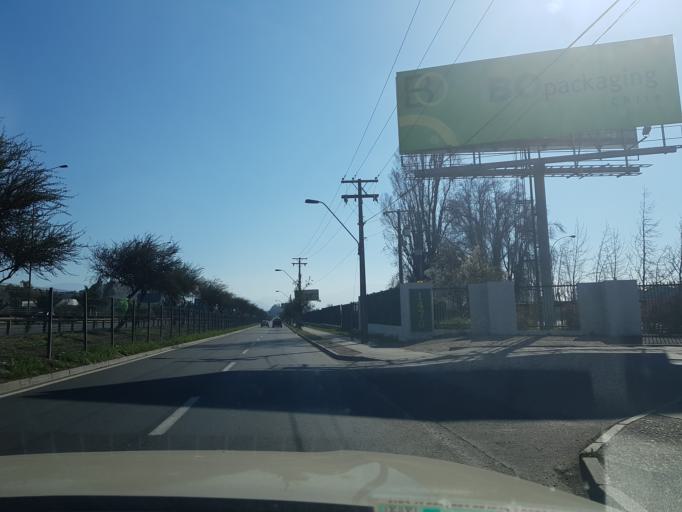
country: CL
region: Santiago Metropolitan
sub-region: Provincia de Santiago
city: Lo Prado
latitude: -33.3728
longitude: -70.7257
